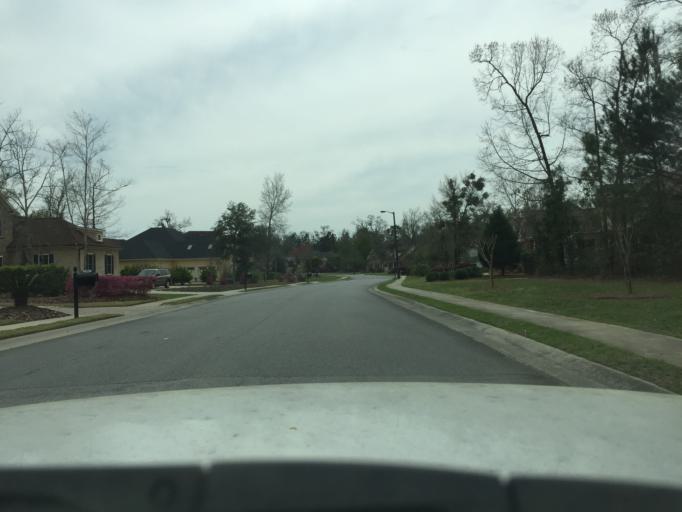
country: US
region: Georgia
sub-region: Chatham County
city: Pooler
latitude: 32.0645
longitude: -81.2441
